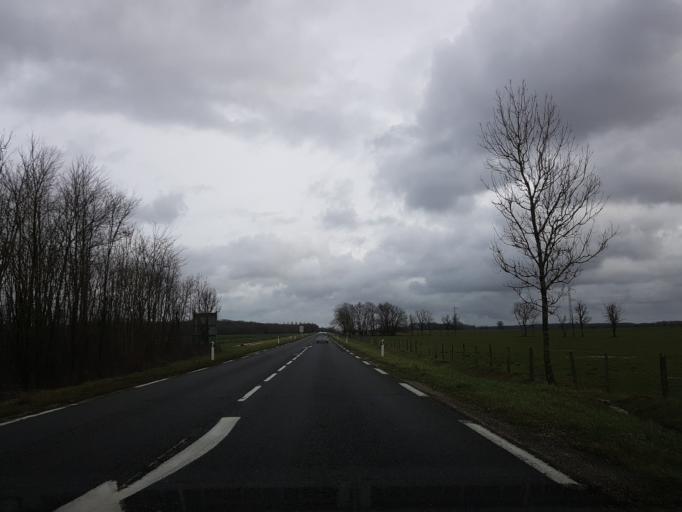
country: FR
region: Champagne-Ardenne
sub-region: Departement de la Haute-Marne
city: Chalindrey
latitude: 47.8155
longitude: 5.5020
